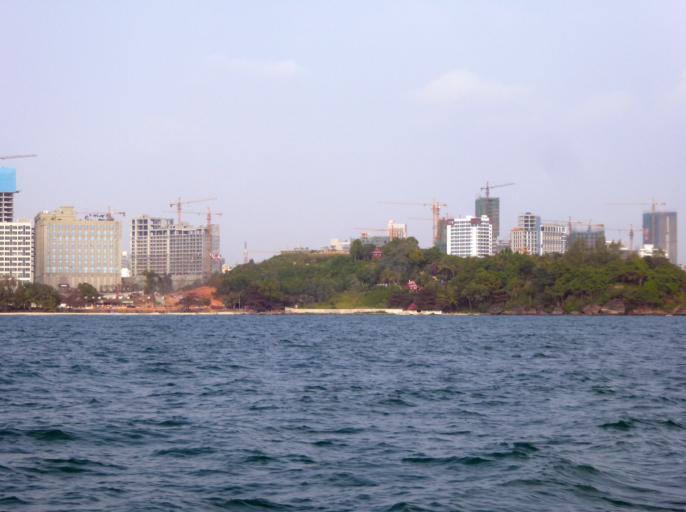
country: KH
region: Preah Sihanouk
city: Sihanoukville
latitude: 10.5999
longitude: 103.5001
